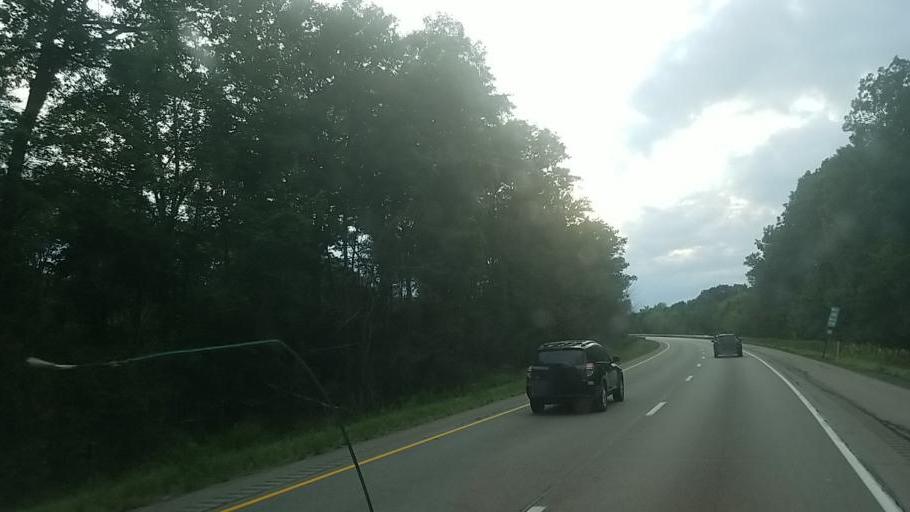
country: US
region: Pennsylvania
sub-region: Clearfield County
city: Shiloh
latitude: 41.0130
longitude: -78.2865
